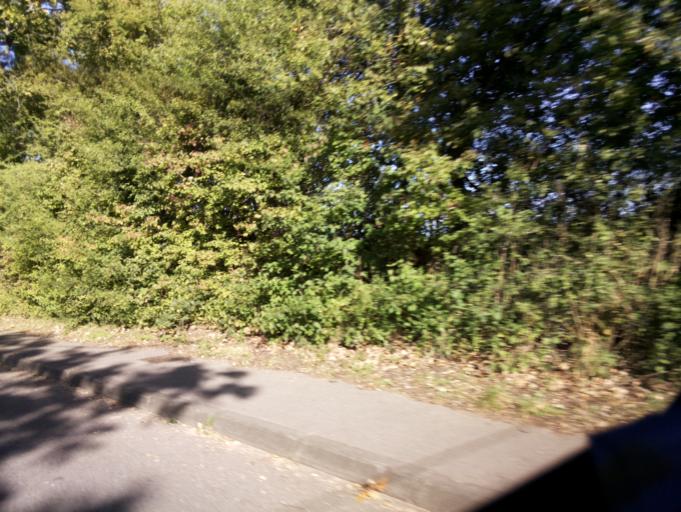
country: GB
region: England
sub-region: West Berkshire
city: Cold Ash
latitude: 51.4153
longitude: -1.2621
